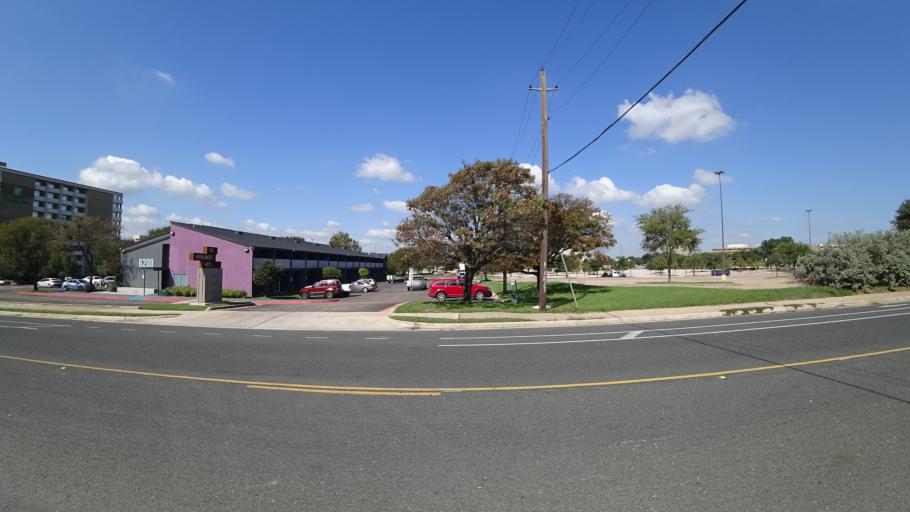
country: US
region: Texas
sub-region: Travis County
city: Austin
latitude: 30.3245
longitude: -97.7095
